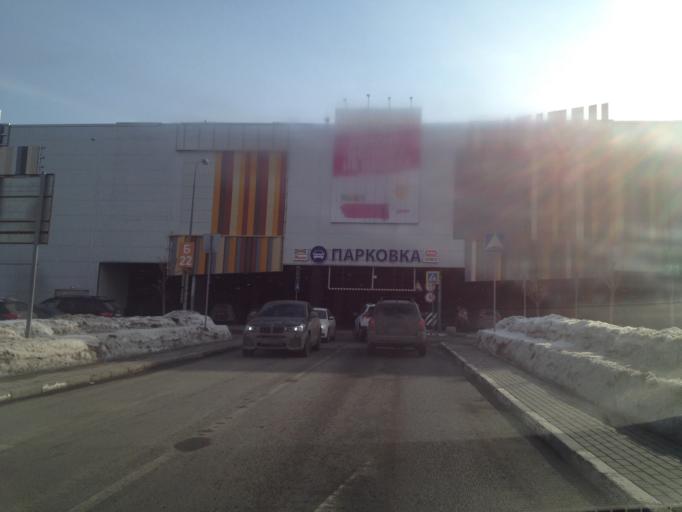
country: RU
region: Sverdlovsk
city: Shirokaya Rechka
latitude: 56.8252
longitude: 60.5069
